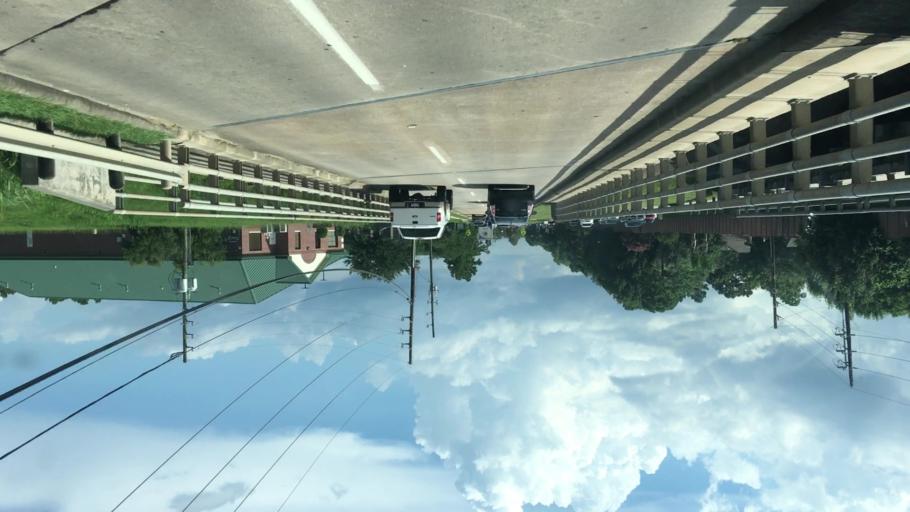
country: US
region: Texas
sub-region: Harris County
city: Atascocita
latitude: 29.9887
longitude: -95.1615
